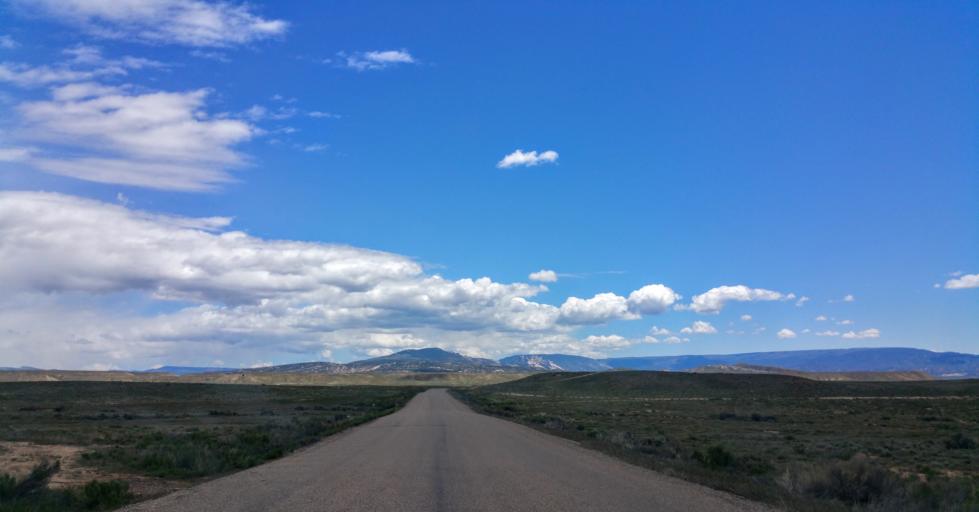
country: US
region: Utah
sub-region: Uintah County
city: Naples
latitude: 40.4647
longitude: -109.4544
